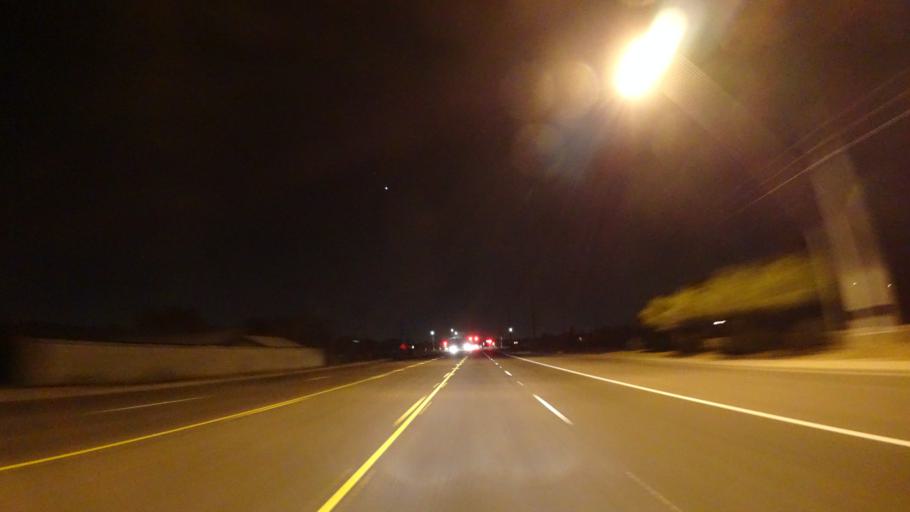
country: US
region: Arizona
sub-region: Pinal County
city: Apache Junction
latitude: 33.4223
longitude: -111.5956
